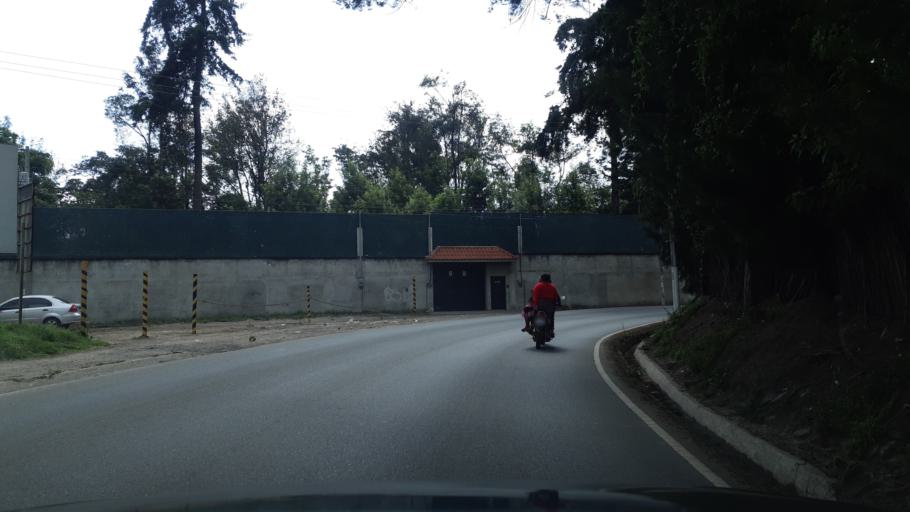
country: GT
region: Chimaltenango
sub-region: Municipio de Chimaltenango
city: Chimaltenango
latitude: 14.6623
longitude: -90.8095
